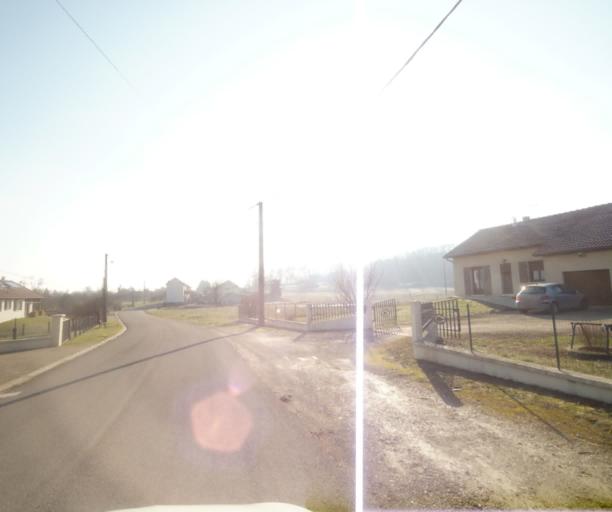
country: FR
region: Champagne-Ardenne
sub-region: Departement de la Haute-Marne
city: Wassy
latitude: 48.5123
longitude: 4.9176
